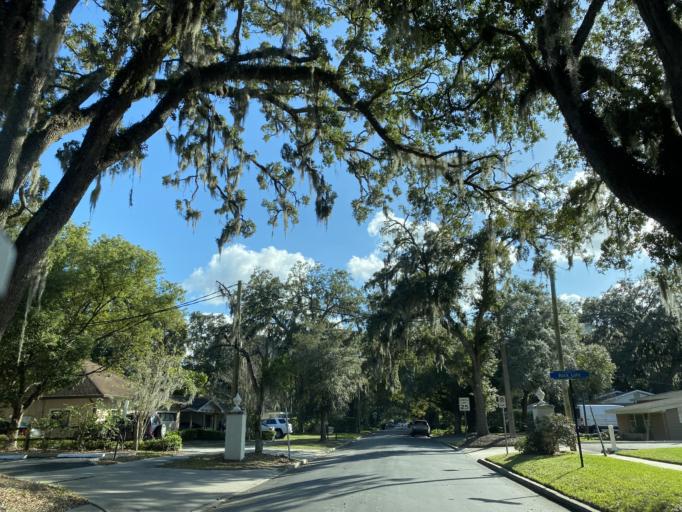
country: US
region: Florida
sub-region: Orange County
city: Orlando
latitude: 28.5528
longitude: -81.4016
